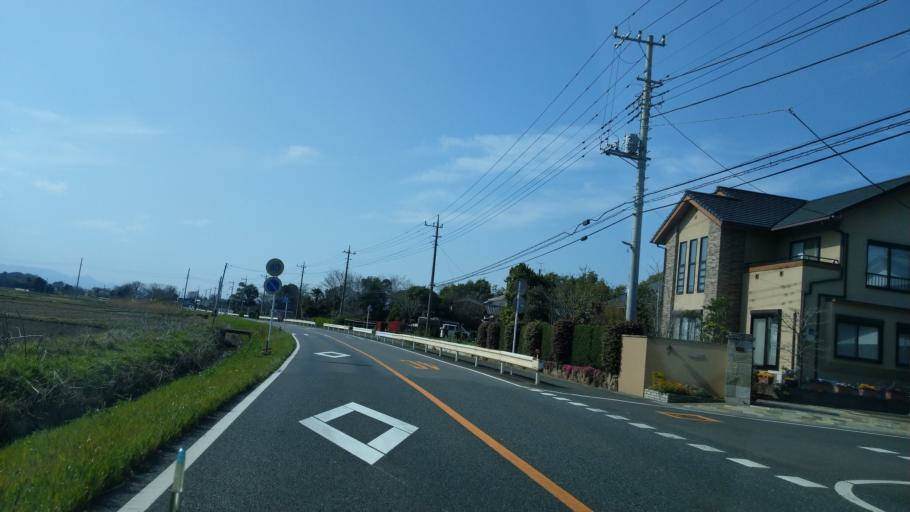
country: JP
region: Saitama
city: Okegawa
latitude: 35.9592
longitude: 139.5238
